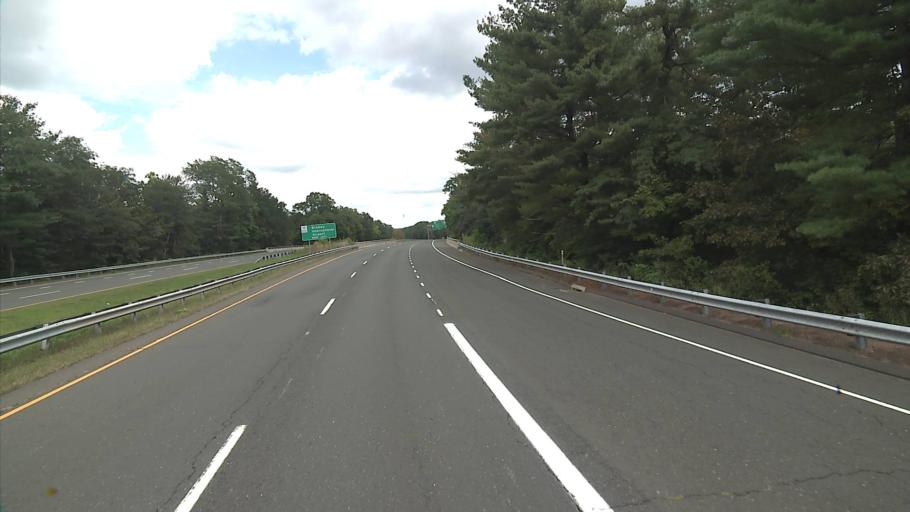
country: US
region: Connecticut
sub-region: Hartford County
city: Tariffville
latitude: 41.8869
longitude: -72.7483
